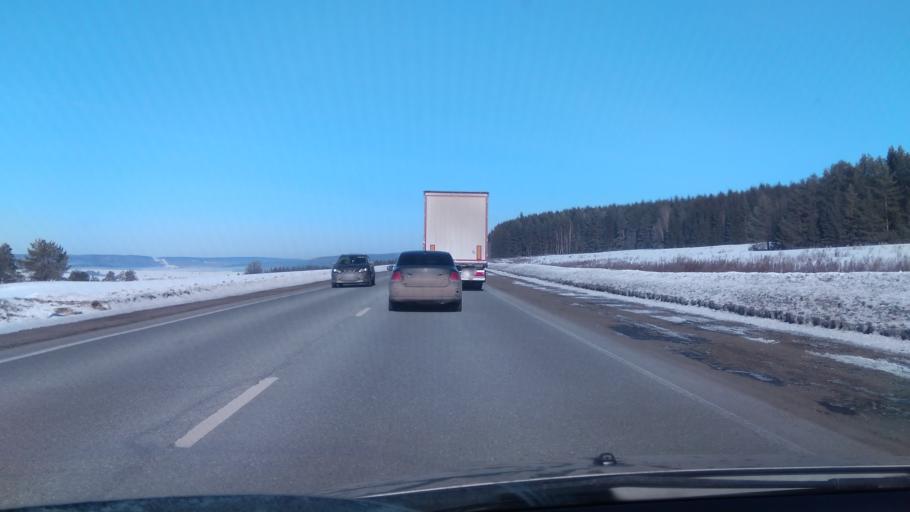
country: RU
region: Perm
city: Suksun
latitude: 57.0309
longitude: 57.4509
